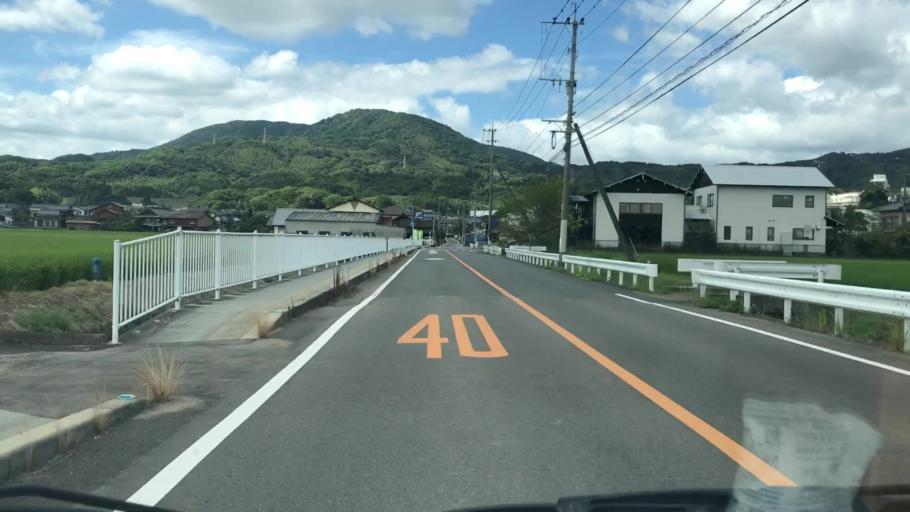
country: JP
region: Saga Prefecture
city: Takeocho-takeo
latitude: 33.2242
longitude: 130.1463
